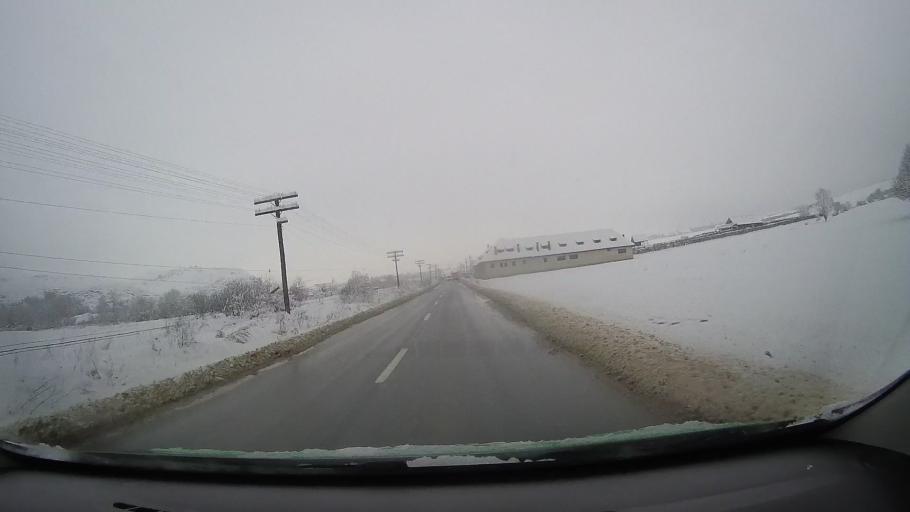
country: RO
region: Sibiu
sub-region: Comuna Orlat
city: Orlat
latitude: 45.7565
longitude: 23.9521
